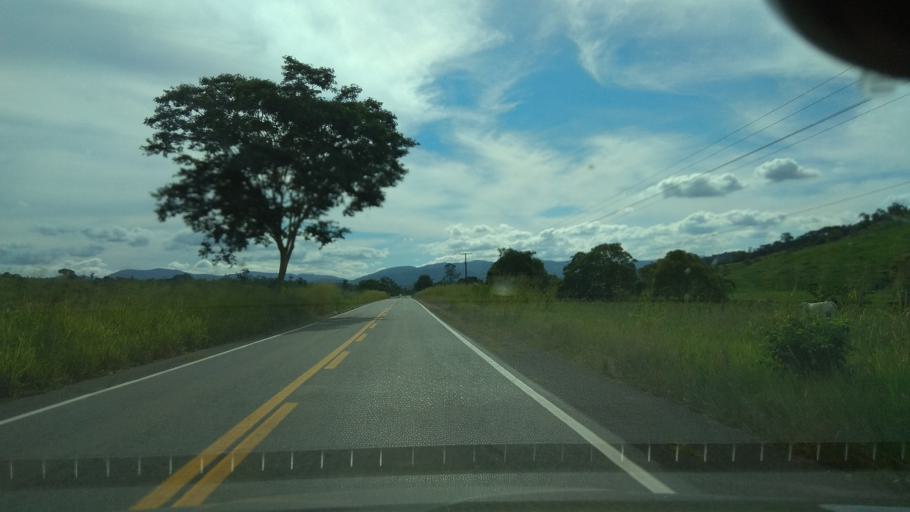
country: BR
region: Bahia
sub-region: Jitauna
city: Jitauna
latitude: -14.0396
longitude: -39.8257
